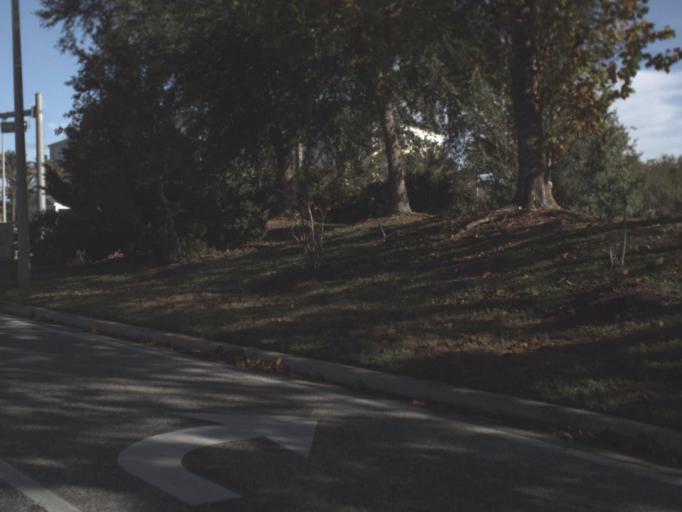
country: US
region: Florida
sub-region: Volusia County
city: Daytona Beach
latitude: 29.1915
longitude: -81.0622
